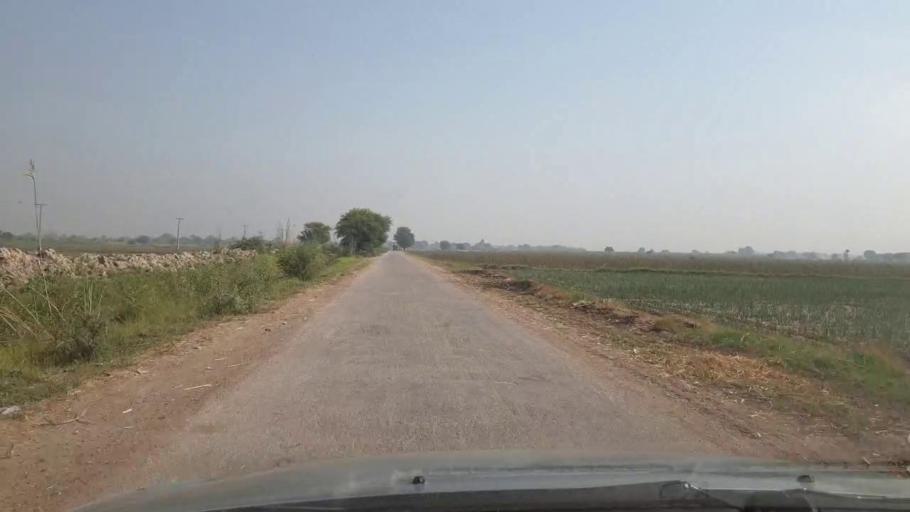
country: PK
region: Sindh
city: Tando Jam
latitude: 25.2904
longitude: 68.5228
